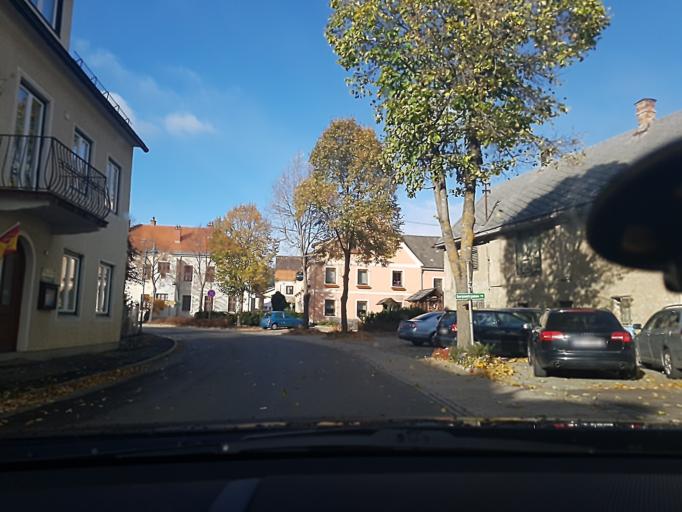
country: AT
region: Styria
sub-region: Politischer Bezirk Murtal
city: Oberzeiring
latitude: 47.2514
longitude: 14.4851
